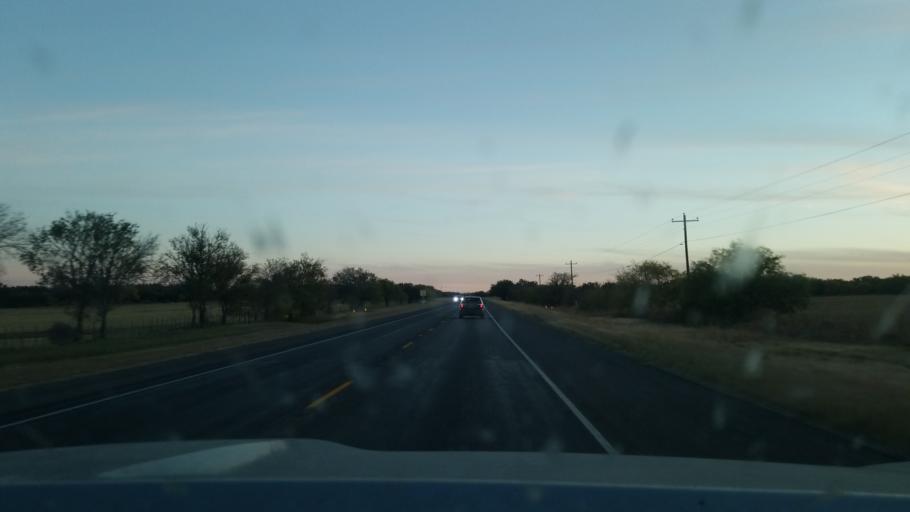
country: US
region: Texas
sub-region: Stephens County
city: Breckenridge
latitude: 32.5886
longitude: -98.8979
